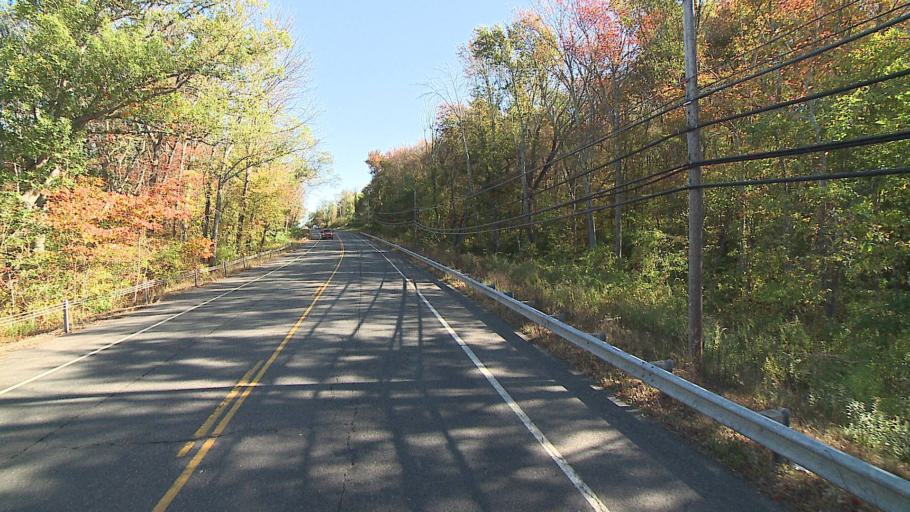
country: US
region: Connecticut
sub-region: Tolland County
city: Hebron
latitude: 41.6842
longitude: -72.3287
